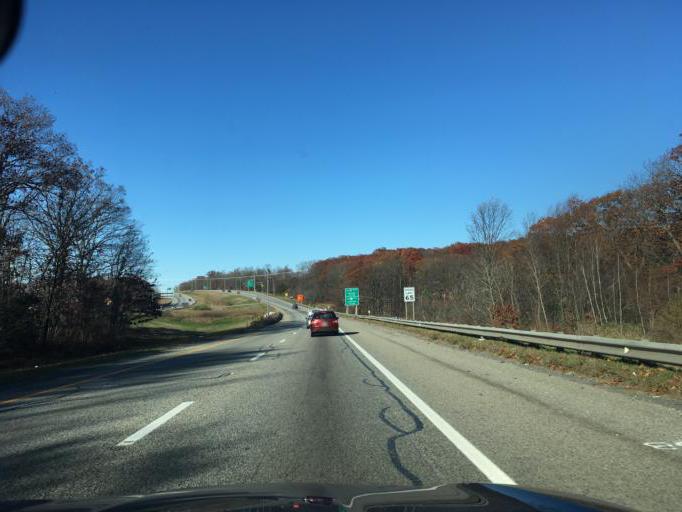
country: US
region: Rhode Island
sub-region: Providence County
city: Johnston
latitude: 41.8097
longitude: -71.5092
